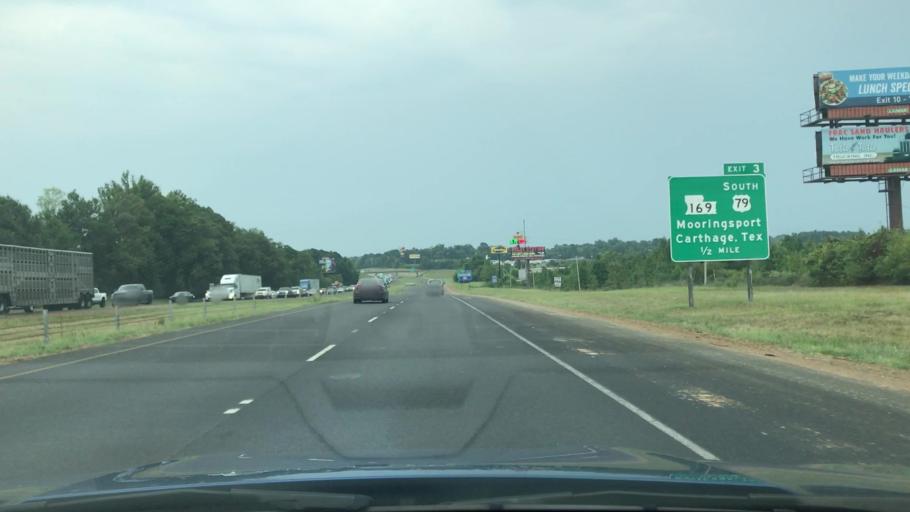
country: US
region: Louisiana
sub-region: Caddo Parish
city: Greenwood
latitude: 32.4495
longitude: -93.9898
